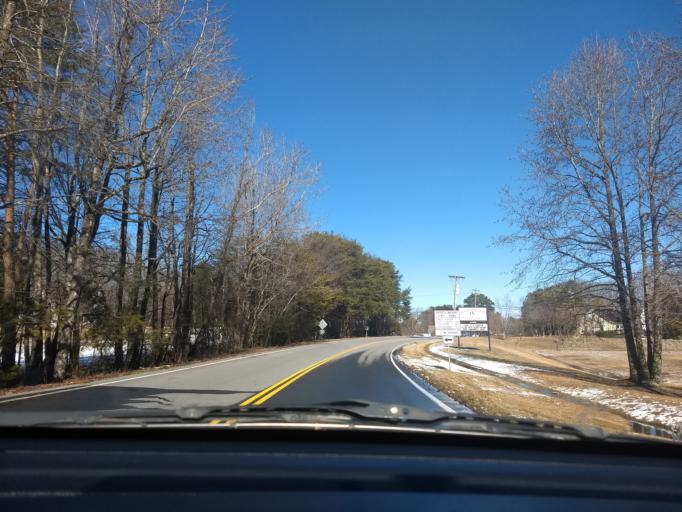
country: US
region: South Carolina
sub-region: Greenville County
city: Wade Hampton
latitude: 34.9131
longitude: -82.3716
